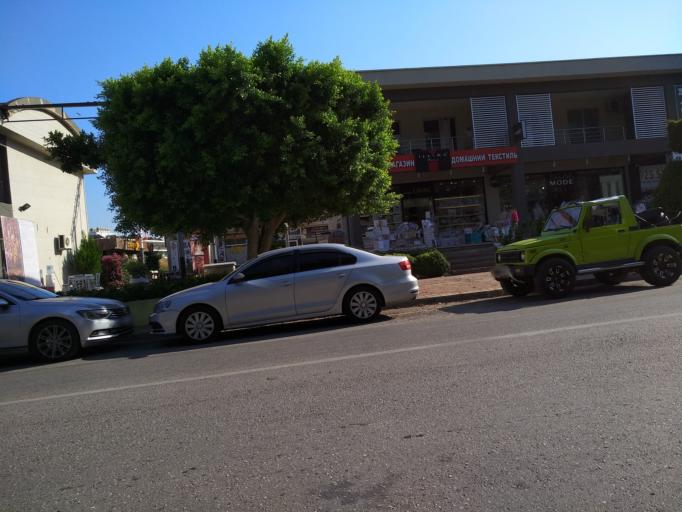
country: TR
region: Antalya
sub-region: Kemer
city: Goeynuek
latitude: 36.6649
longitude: 30.5569
